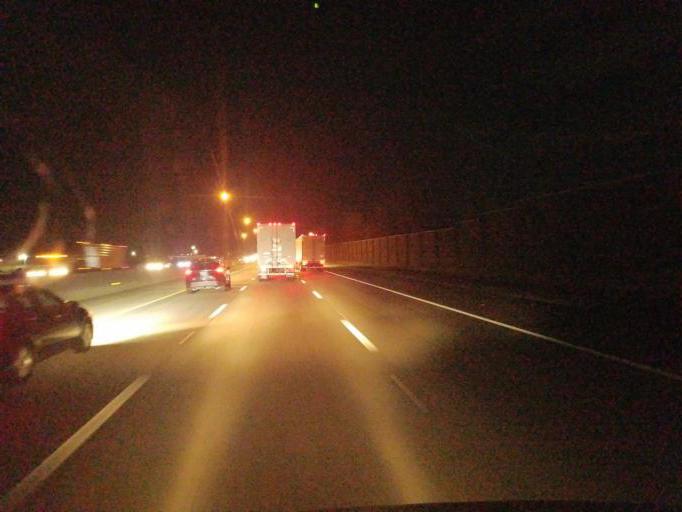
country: US
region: Ohio
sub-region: Montgomery County
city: Huber Heights
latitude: 39.8681
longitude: -84.1086
